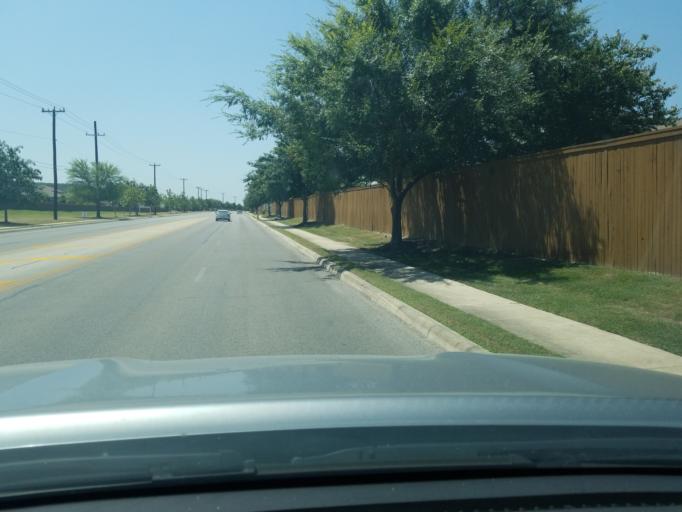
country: US
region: Texas
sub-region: Bexar County
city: Timberwood Park
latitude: 29.7065
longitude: -98.4835
